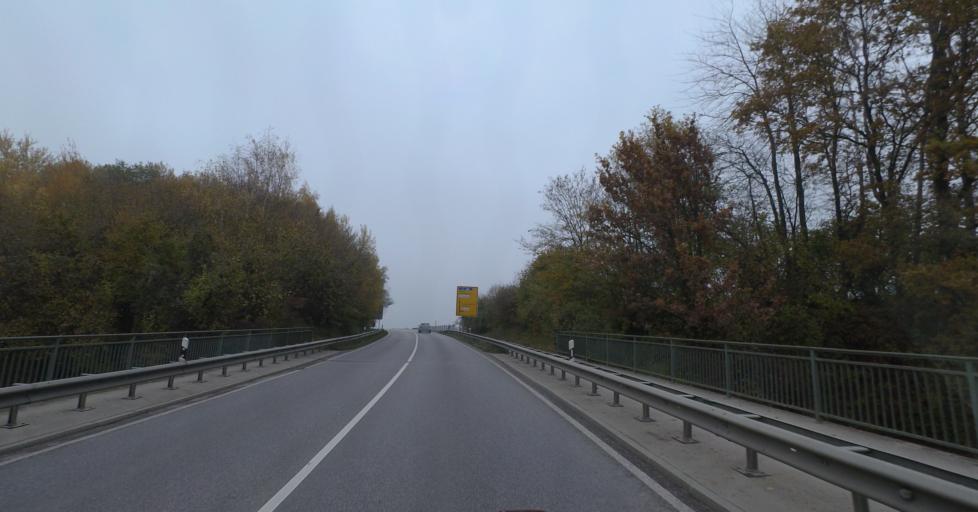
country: DE
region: Bavaria
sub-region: Upper Bavaria
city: Unterneukirchen
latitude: 48.1537
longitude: 12.6128
